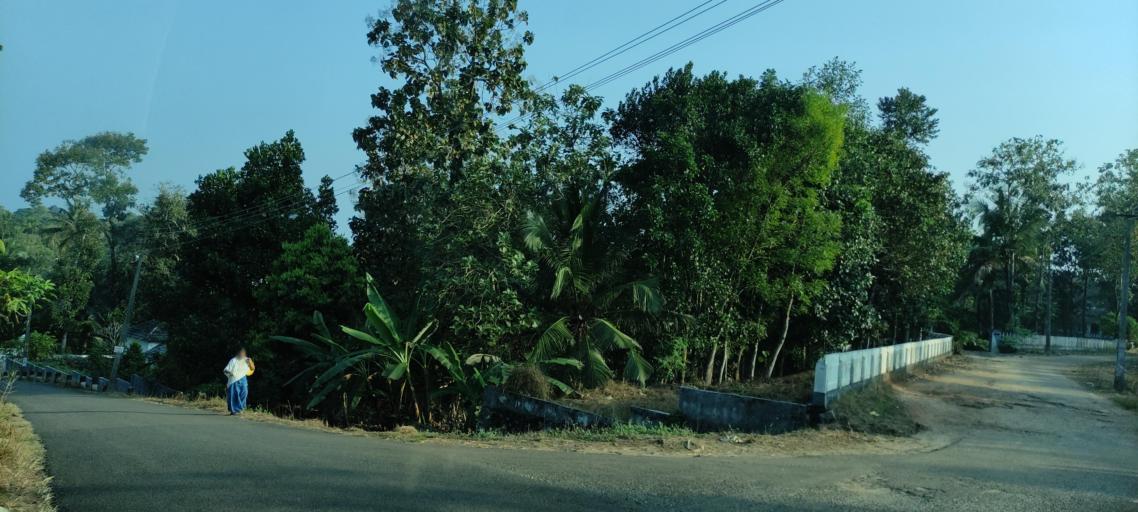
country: IN
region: Kerala
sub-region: Pattanamtitta
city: Adur
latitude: 9.1360
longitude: 76.7337
